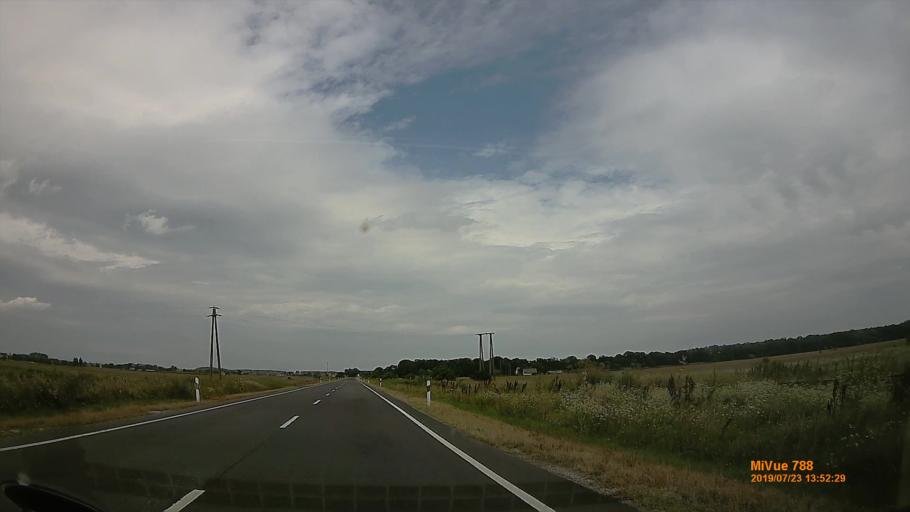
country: HU
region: Hajdu-Bihar
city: Polgar
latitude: 47.9027
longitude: 21.1613
